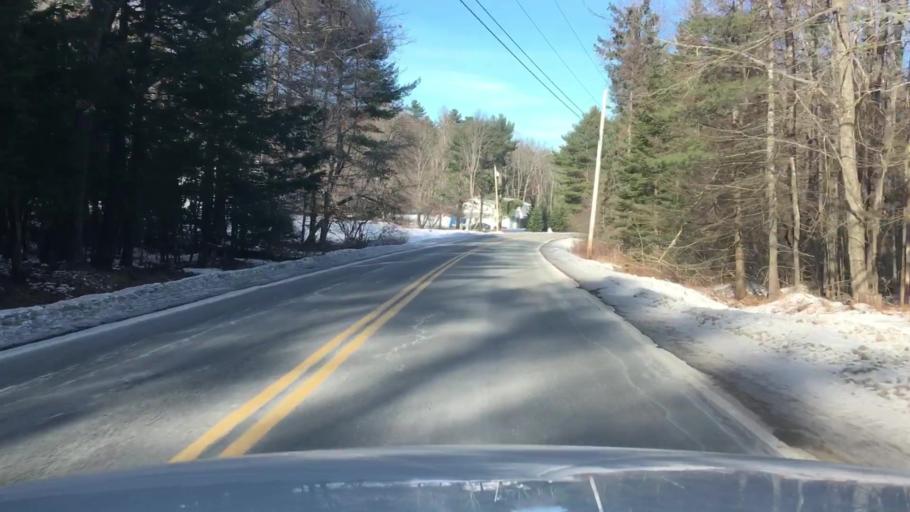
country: US
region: Maine
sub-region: Hancock County
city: Dedham
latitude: 44.6385
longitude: -68.6993
